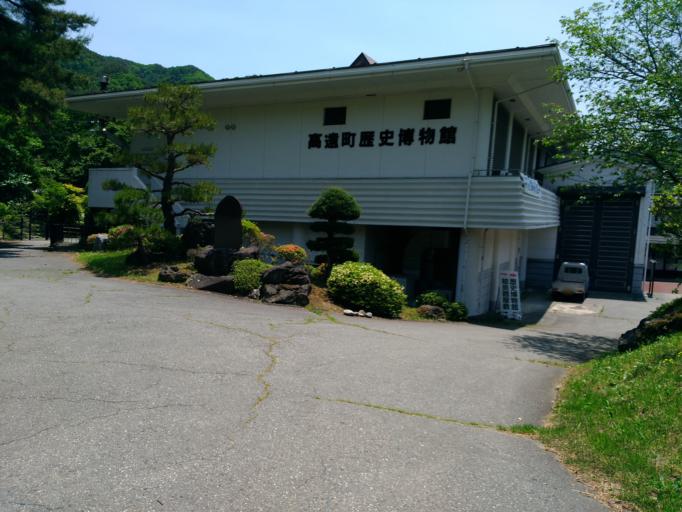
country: JP
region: Nagano
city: Ina
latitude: 35.8305
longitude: 138.0638
